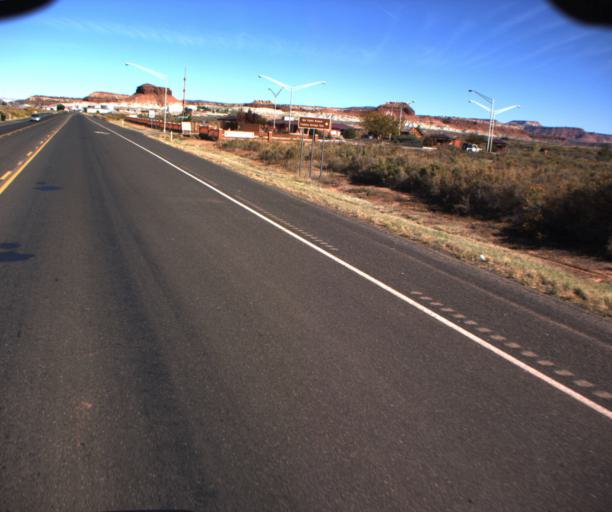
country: US
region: Arizona
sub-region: Coconino County
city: Fredonia
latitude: 36.9615
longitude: -112.5269
